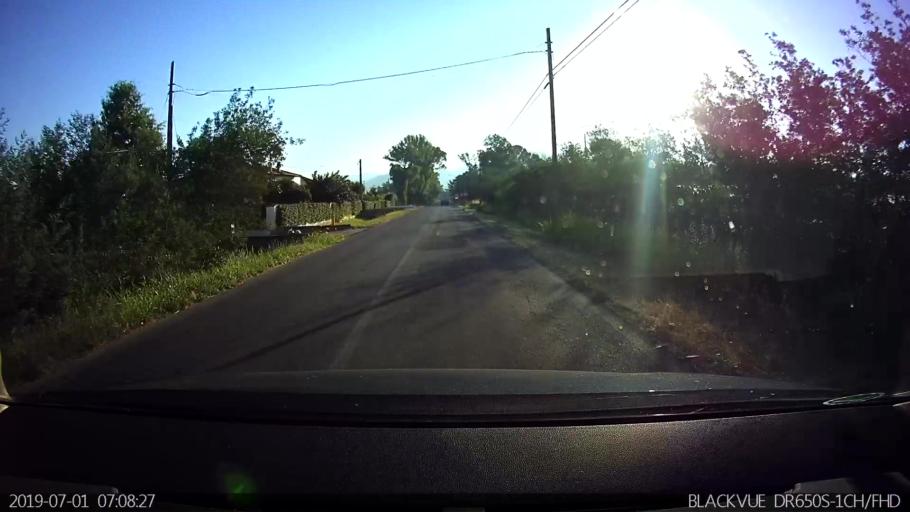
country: IT
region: Latium
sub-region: Provincia di Latina
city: Borgo Hermada
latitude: 41.2975
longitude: 13.1504
